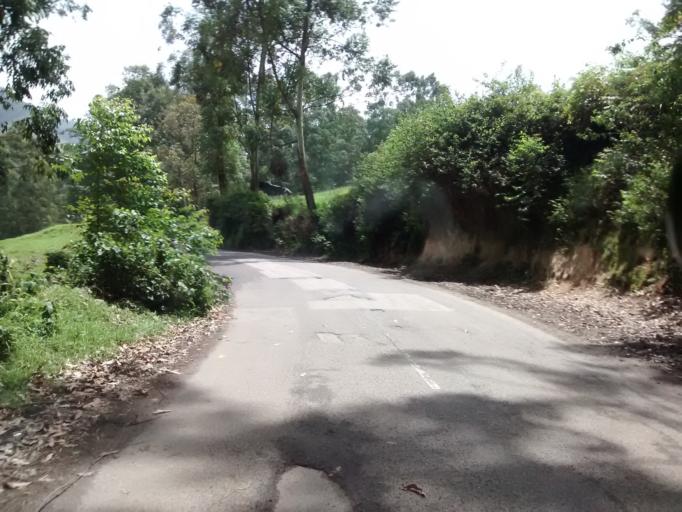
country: IN
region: Kerala
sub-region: Idukki
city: Munnar
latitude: 10.1151
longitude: 77.1373
